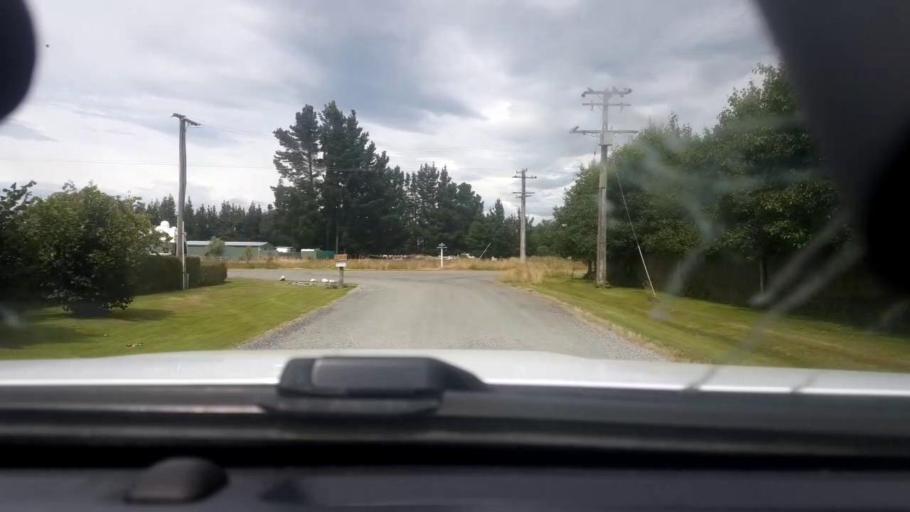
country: NZ
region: Canterbury
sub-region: Timaru District
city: Pleasant Point
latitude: -44.1442
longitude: 171.2884
